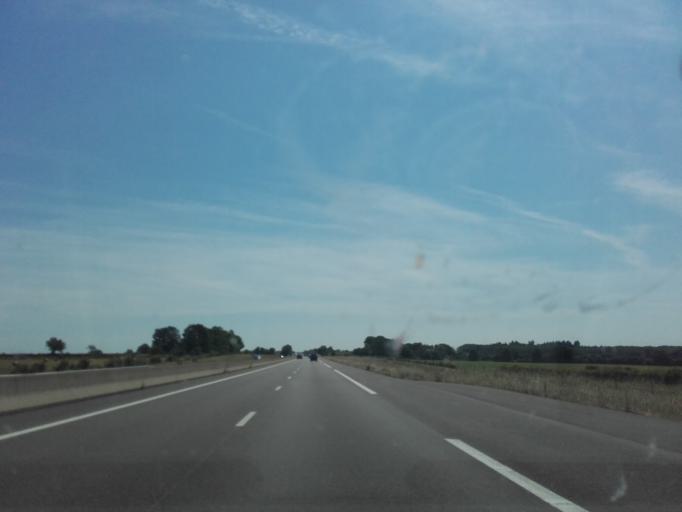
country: FR
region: Bourgogne
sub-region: Departement de la Cote-d'Or
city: Semur-en-Auxois
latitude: 47.4796
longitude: 4.1858
